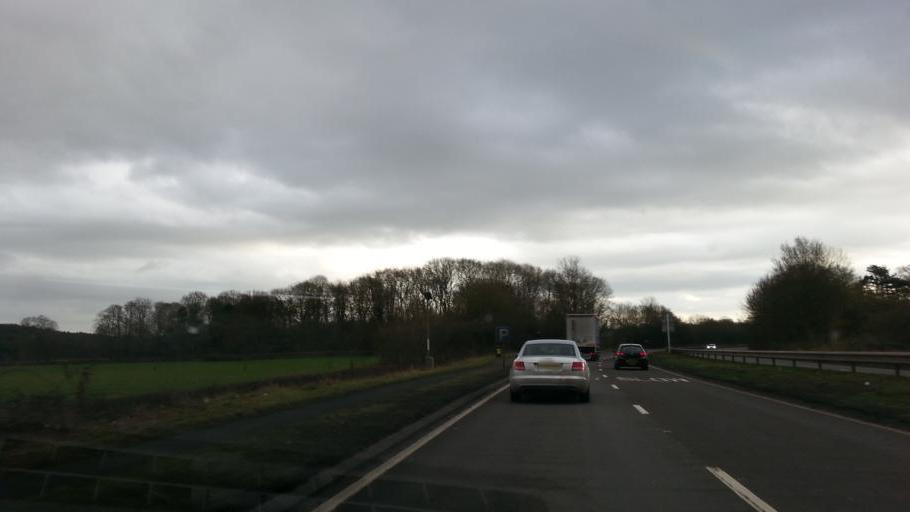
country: GB
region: England
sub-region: Staffordshire
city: Lichfield
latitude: 52.6603
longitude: -1.8119
